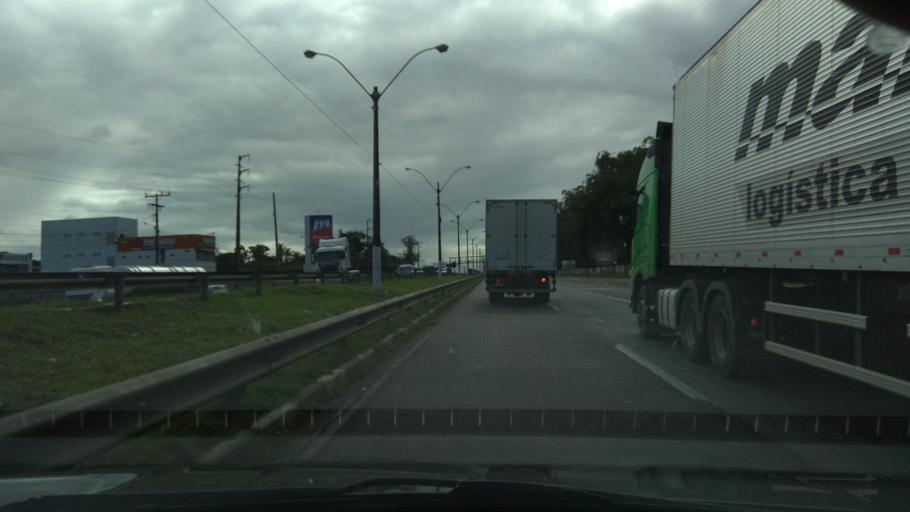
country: BR
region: Bahia
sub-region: Feira De Santana
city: Feira de Santana
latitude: -12.2980
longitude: -38.9014
